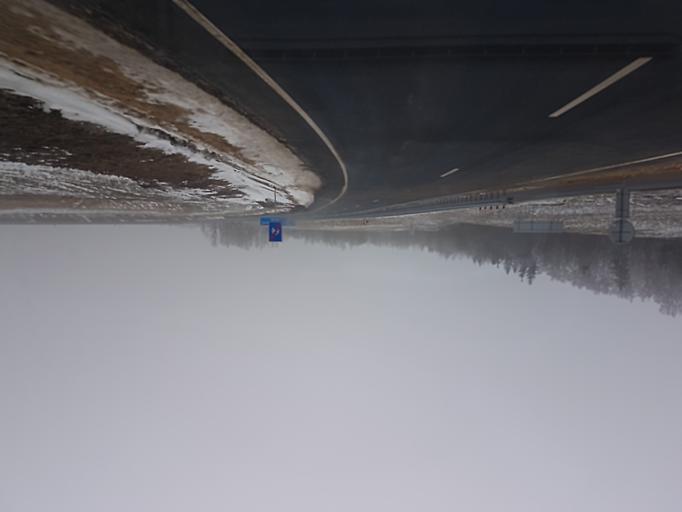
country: BY
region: Minsk
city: Samakhvalavichy
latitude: 53.7062
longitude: 27.4513
